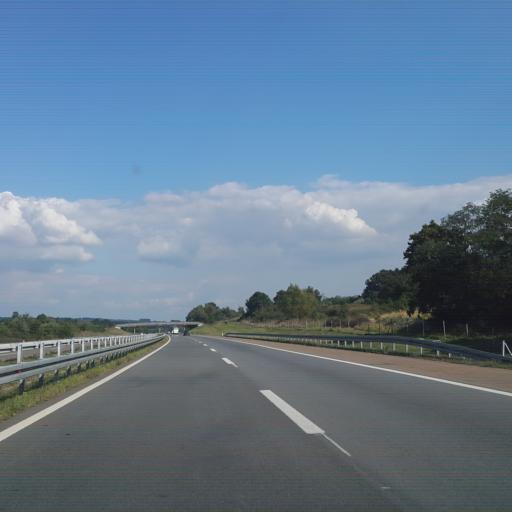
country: RS
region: Central Serbia
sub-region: Podunavski Okrug
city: Smederevo
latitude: 44.5843
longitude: 20.8432
